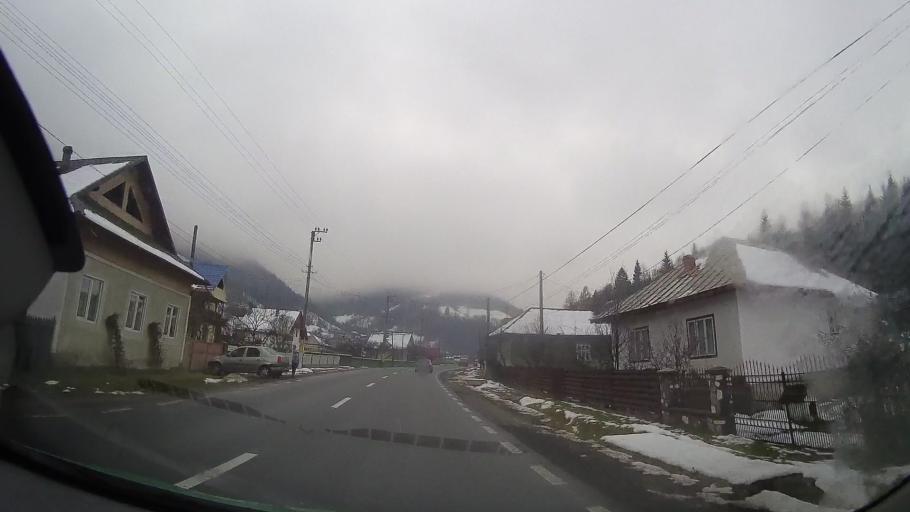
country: RO
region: Neamt
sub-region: Comuna Bicazu Ardelean
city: Bicazu Ardelean
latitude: 46.8581
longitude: 25.9365
